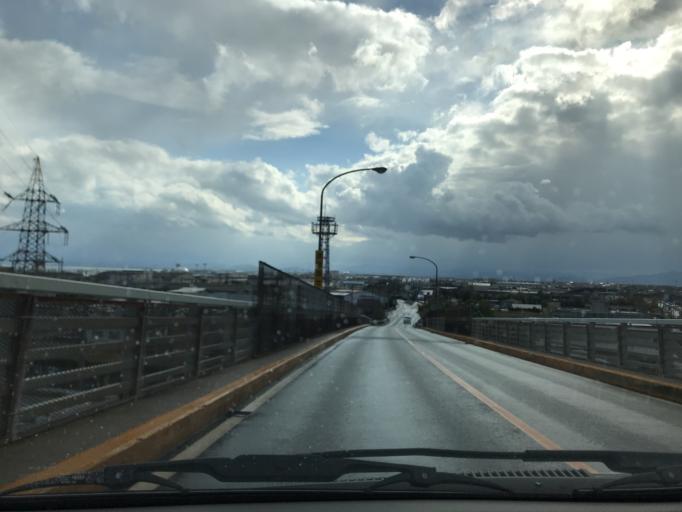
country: JP
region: Shimane
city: Sakaiminato
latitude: 35.5457
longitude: 133.2458
